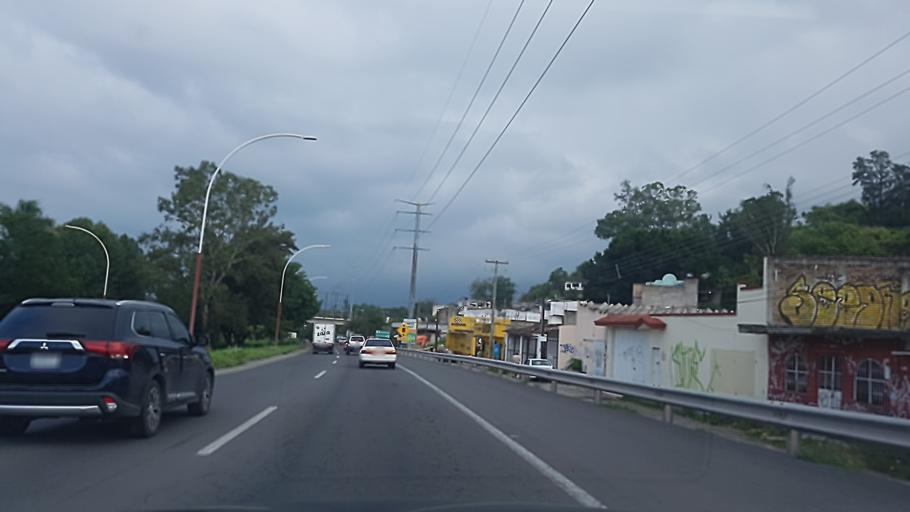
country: MX
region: Nayarit
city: Xalisco
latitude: 21.4735
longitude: -104.8923
